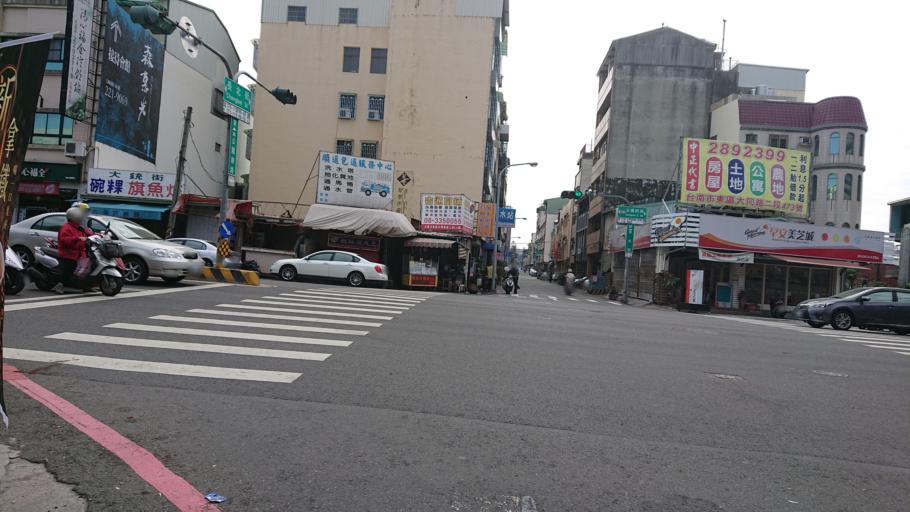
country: TW
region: Taiwan
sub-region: Tainan
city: Tainan
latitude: 23.0023
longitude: 120.2046
